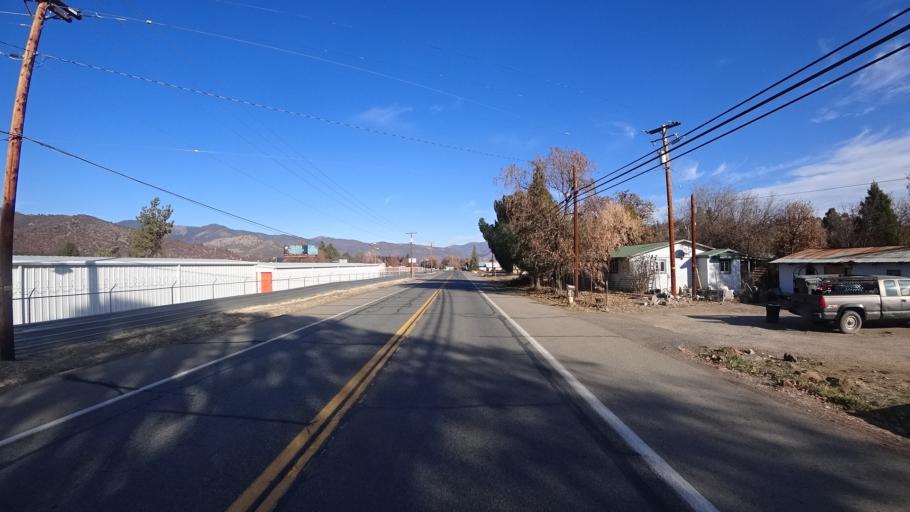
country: US
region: California
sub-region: Siskiyou County
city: Yreka
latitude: 41.6964
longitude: -122.6391
